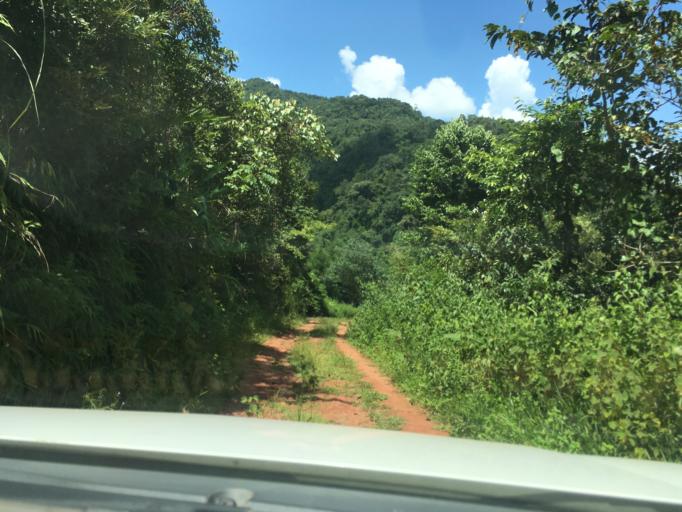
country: LA
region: Phongsali
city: Phongsali
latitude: 21.7893
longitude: 101.8662
